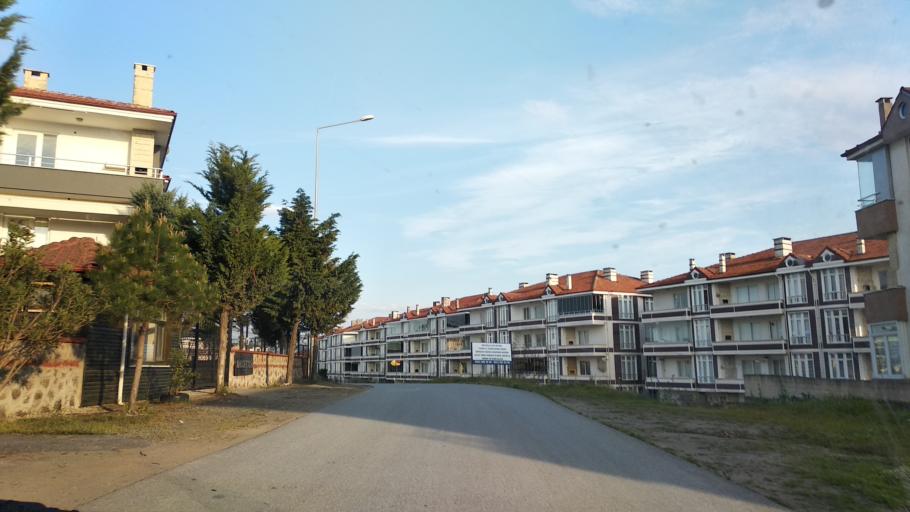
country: TR
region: Sakarya
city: Karasu
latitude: 41.0963
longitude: 30.7236
